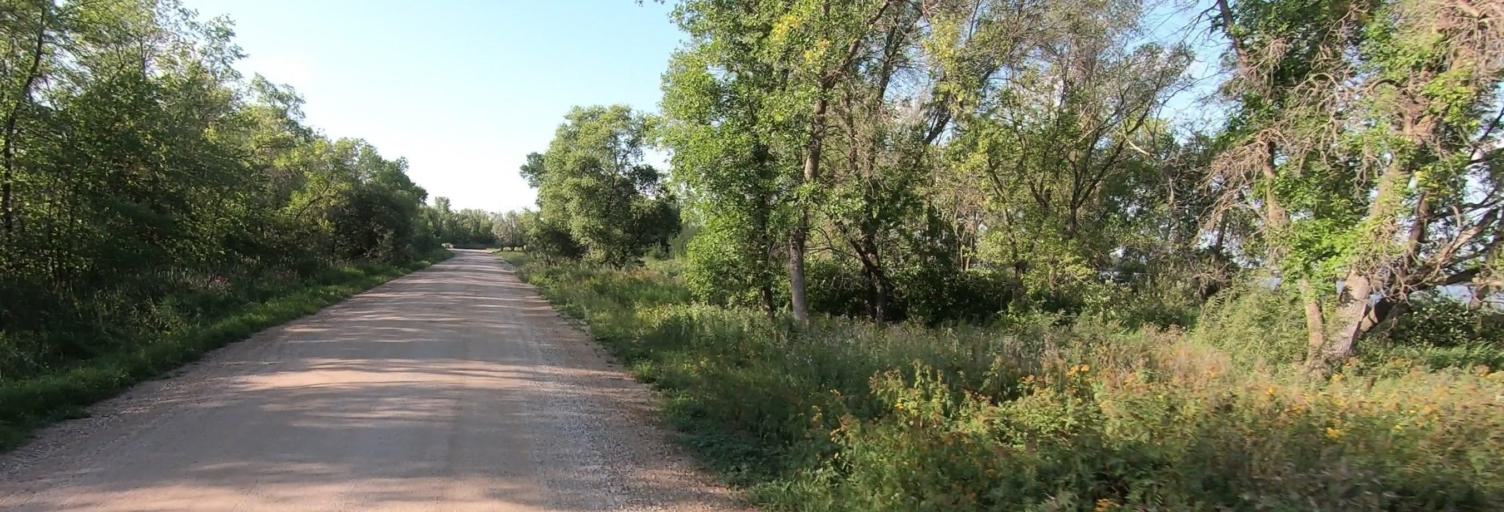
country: CA
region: Manitoba
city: Selkirk
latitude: 50.2900
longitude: -96.8660
